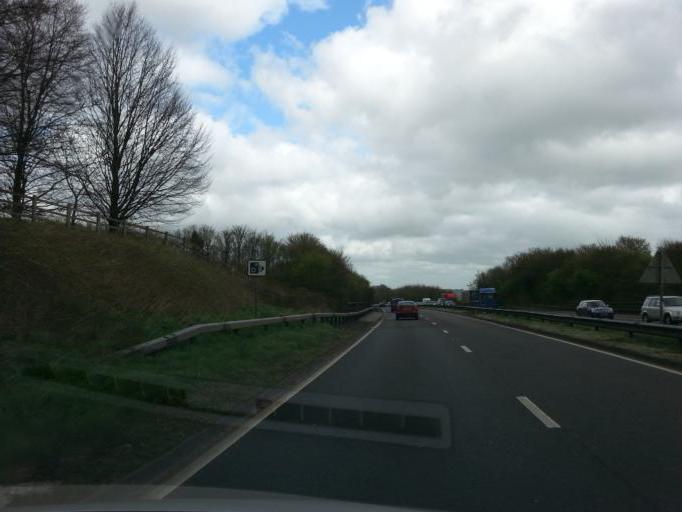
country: GB
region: England
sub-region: Wiltshire
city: Stockton
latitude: 51.1289
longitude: -2.0126
